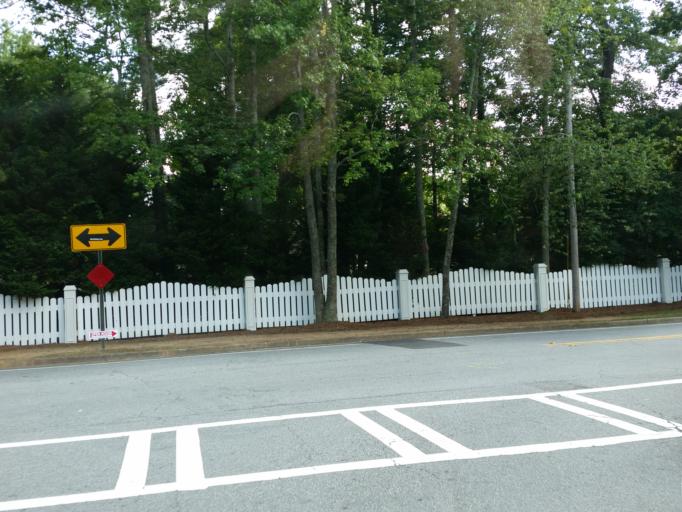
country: US
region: Georgia
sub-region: Fulton County
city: Roswell
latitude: 34.0265
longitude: -84.4429
